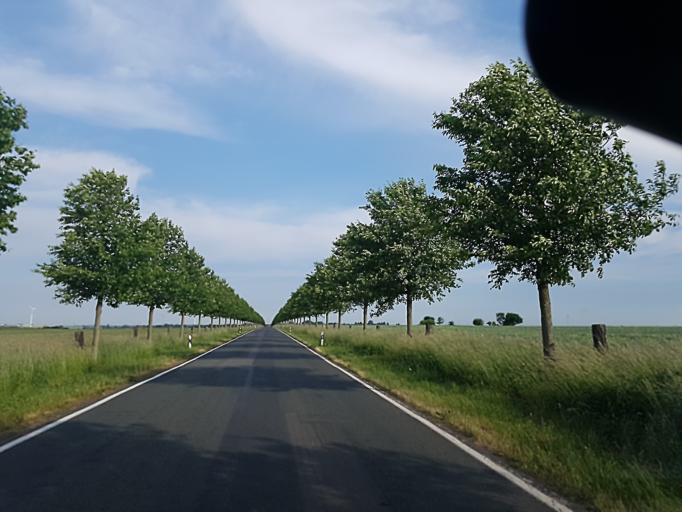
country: DE
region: Saxony-Anhalt
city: Kropstadt
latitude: 51.9895
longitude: 12.7949
